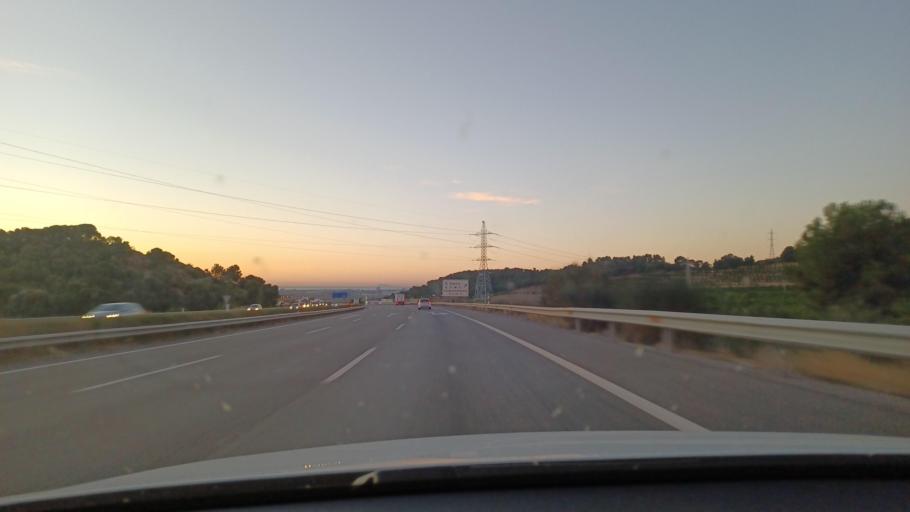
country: ES
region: Valencia
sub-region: Provincia de Valencia
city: Petres
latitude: 39.6558
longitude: -0.3051
